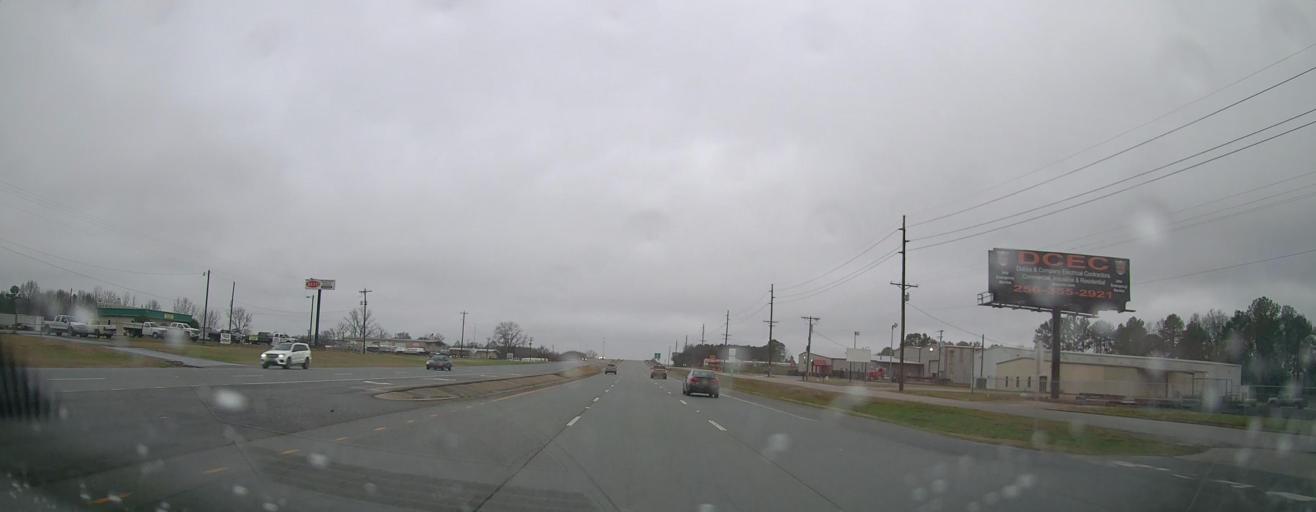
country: US
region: Alabama
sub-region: Morgan County
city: Decatur
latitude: 34.6146
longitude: -87.0311
